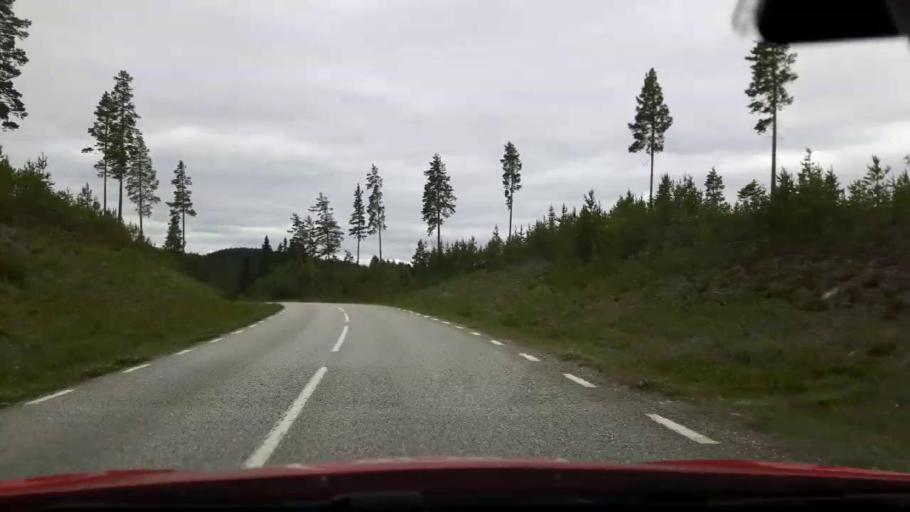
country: SE
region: Jaemtland
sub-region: Stroemsunds Kommun
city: Stroemsund
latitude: 63.3626
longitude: 15.7139
